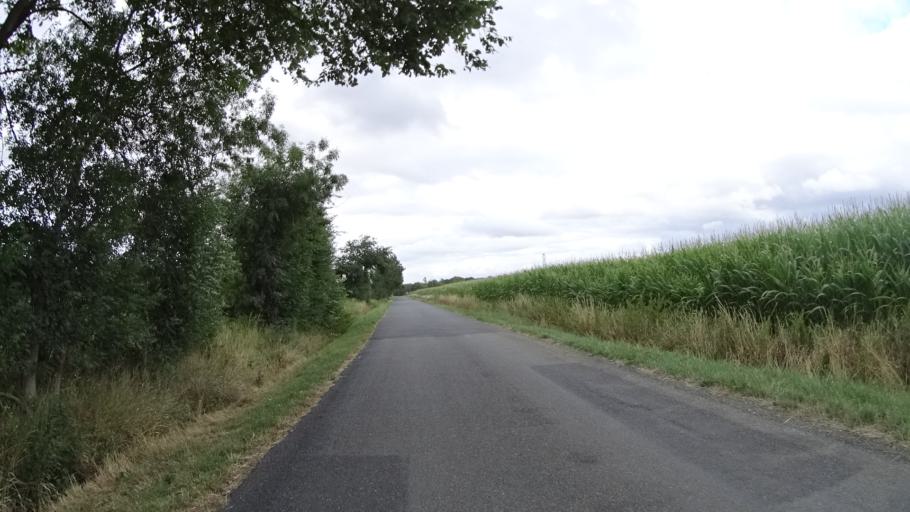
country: FR
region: Pays de la Loire
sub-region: Departement de la Loire-Atlantique
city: Saint-Gereon
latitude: 47.3577
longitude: -1.2182
